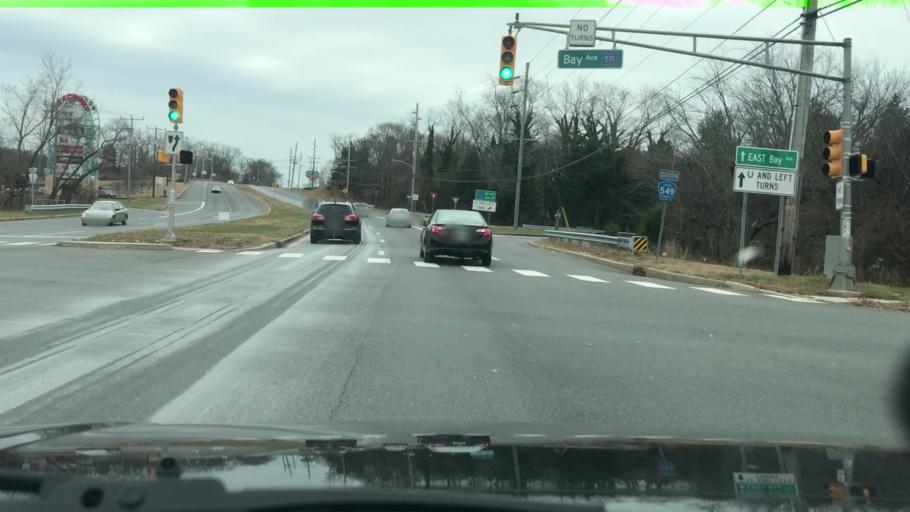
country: US
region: New Jersey
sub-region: Ocean County
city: Toms River
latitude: 39.9790
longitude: -74.1829
